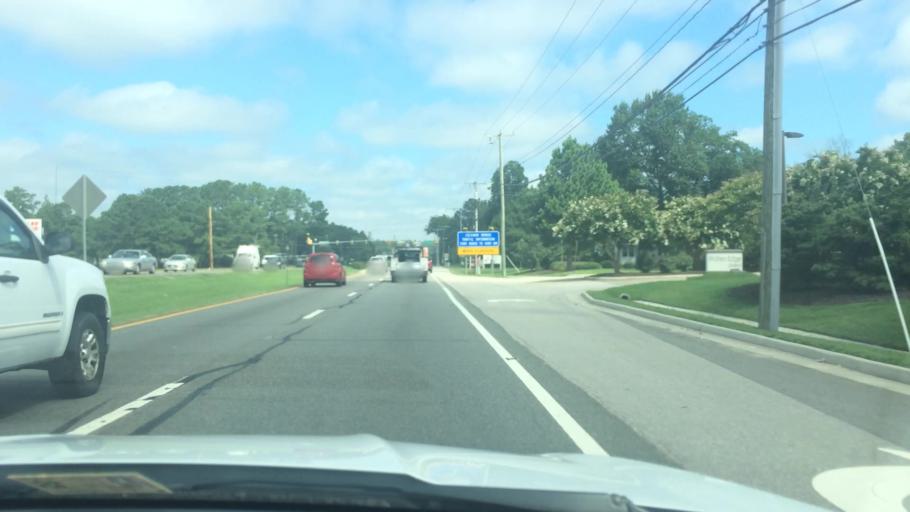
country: US
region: Virginia
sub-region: York County
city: Yorktown
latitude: 37.1761
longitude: -76.4775
